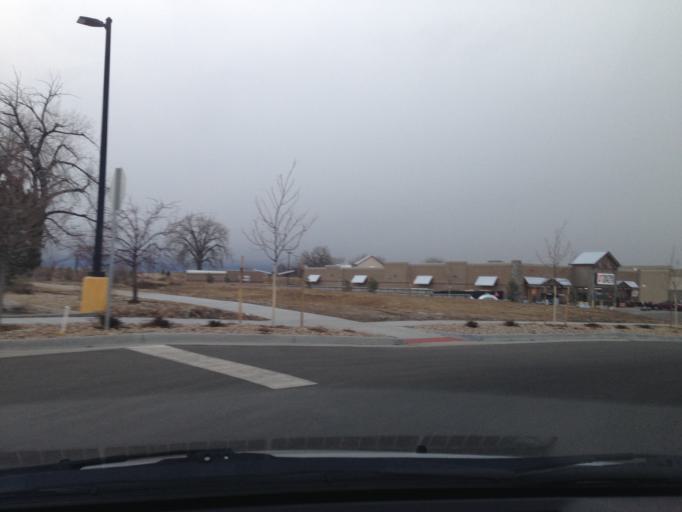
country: US
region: Colorado
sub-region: Boulder County
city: Lafayette
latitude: 40.0073
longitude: -105.1044
